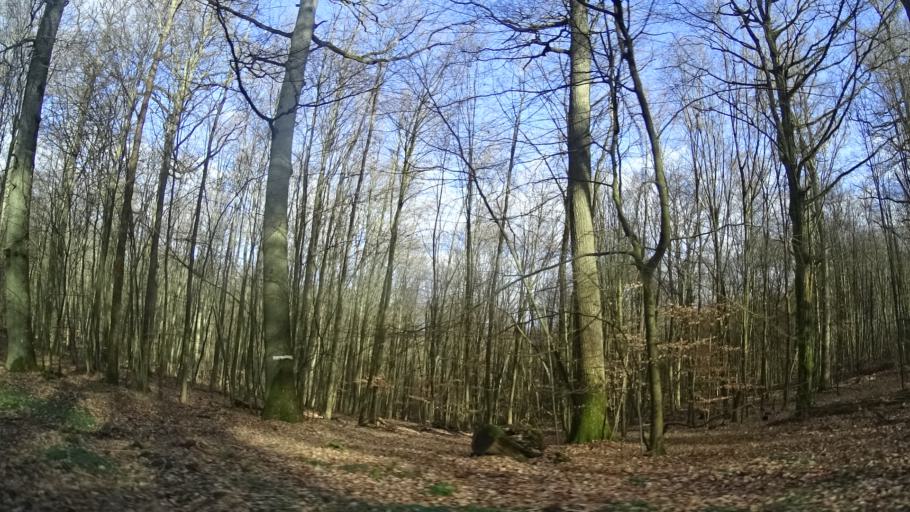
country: DE
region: Hesse
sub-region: Regierungsbezirk Darmstadt
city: Wiesbaden
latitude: 50.1092
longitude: 8.2414
